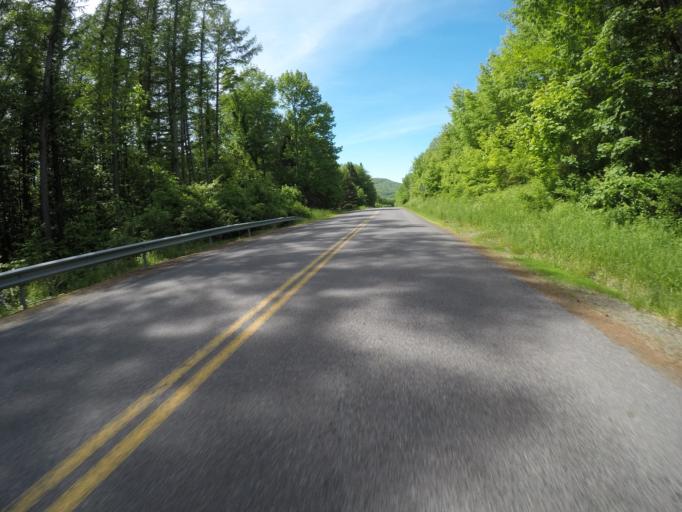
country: US
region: New York
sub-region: Sullivan County
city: Livingston Manor
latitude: 42.0915
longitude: -74.8210
